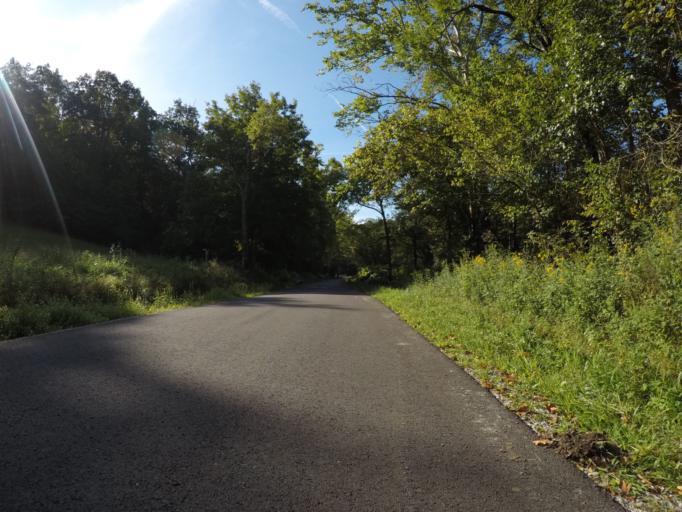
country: US
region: Ohio
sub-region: Lawrence County
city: Burlington
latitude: 38.5068
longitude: -82.5209
